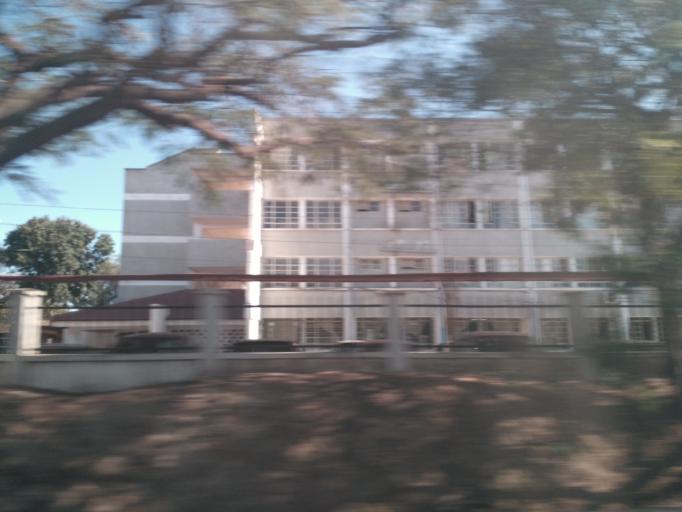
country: TZ
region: Dodoma
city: Dodoma
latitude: -6.1837
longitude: 35.7451
